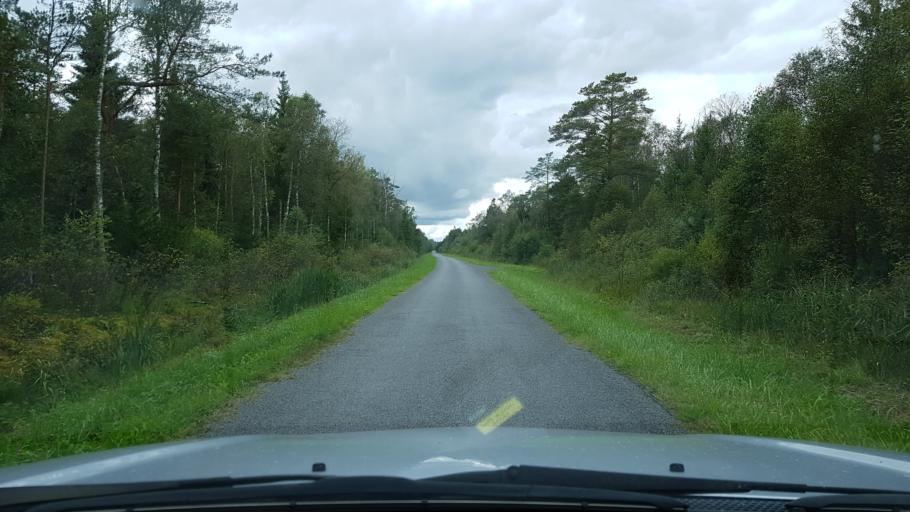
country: EE
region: Harju
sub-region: Rae vald
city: Vaida
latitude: 59.3018
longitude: 25.0270
